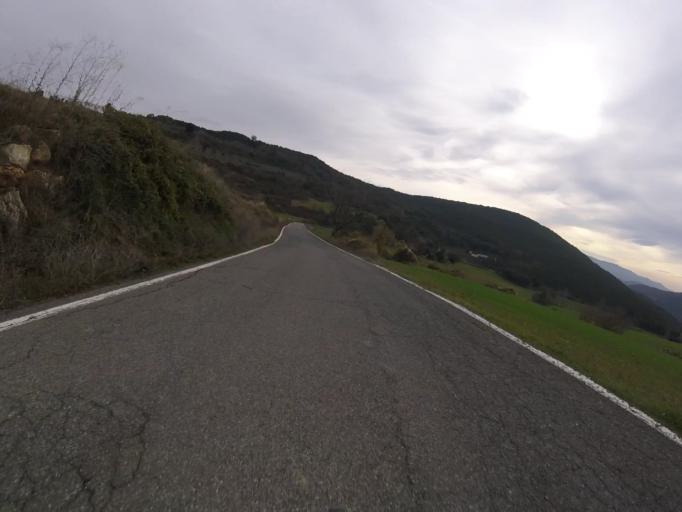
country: ES
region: Navarre
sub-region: Provincia de Navarra
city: Estella
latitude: 42.7149
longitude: -2.0469
